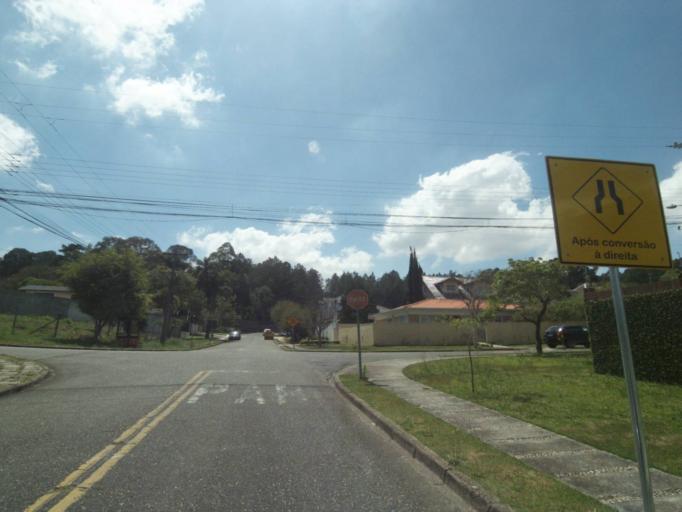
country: BR
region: Parana
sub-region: Curitiba
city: Curitiba
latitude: -25.4097
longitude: -49.2352
